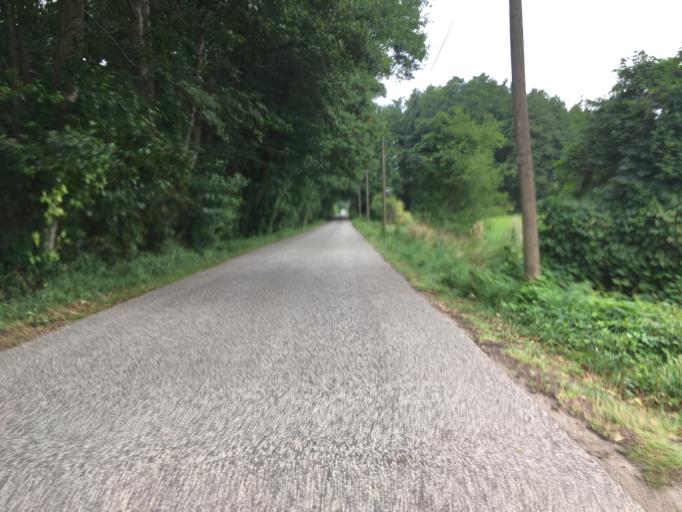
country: DE
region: Brandenburg
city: Gerswalde
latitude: 53.1629
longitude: 13.8460
